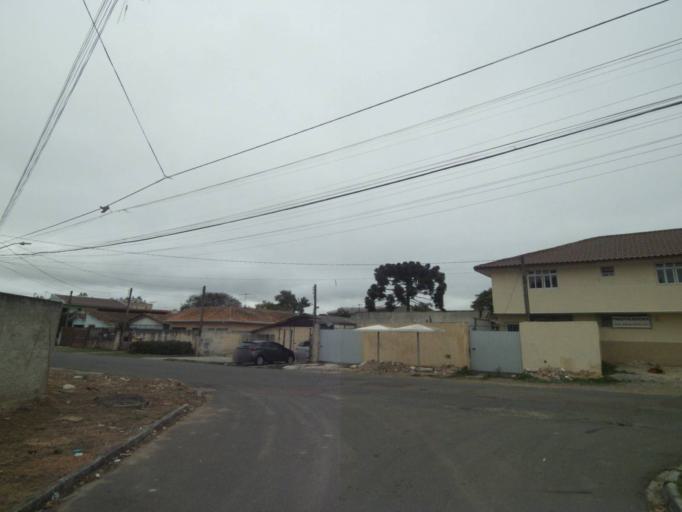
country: BR
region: Parana
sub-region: Curitiba
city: Curitiba
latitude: -25.4662
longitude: -49.2683
